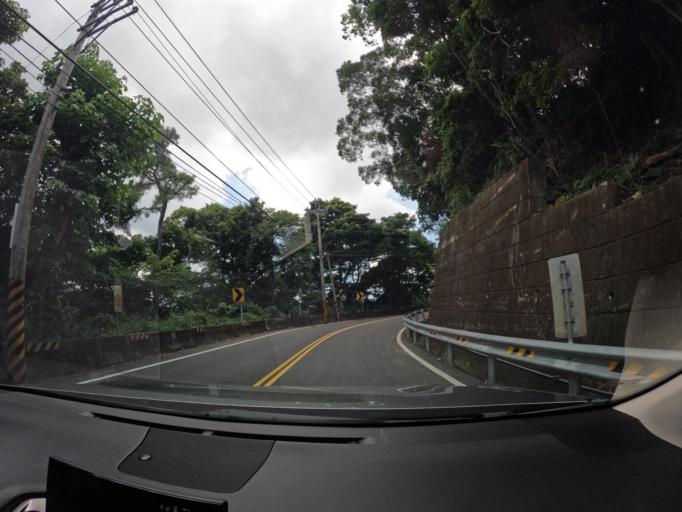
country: TW
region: Taiwan
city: Fengyuan
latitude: 24.3843
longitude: 120.8128
